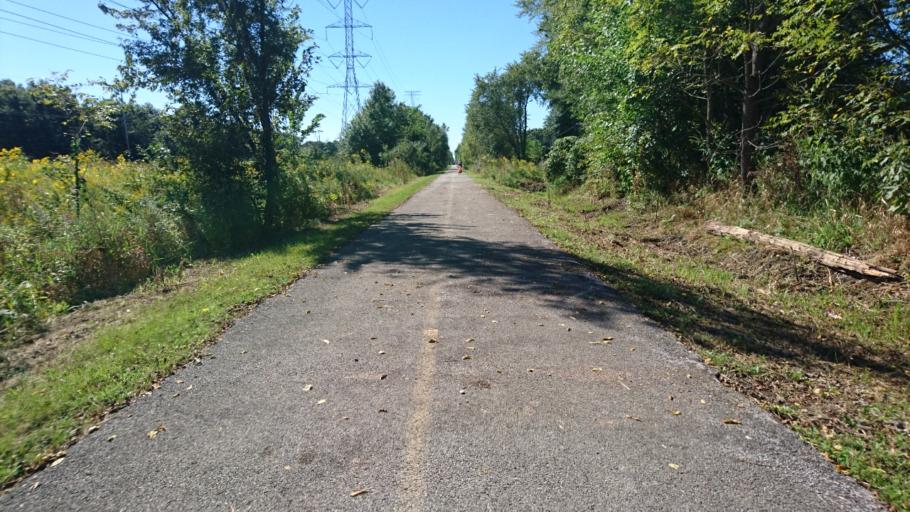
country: US
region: Illinois
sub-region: Cook County
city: Calumet City
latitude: 41.6113
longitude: -87.5494
